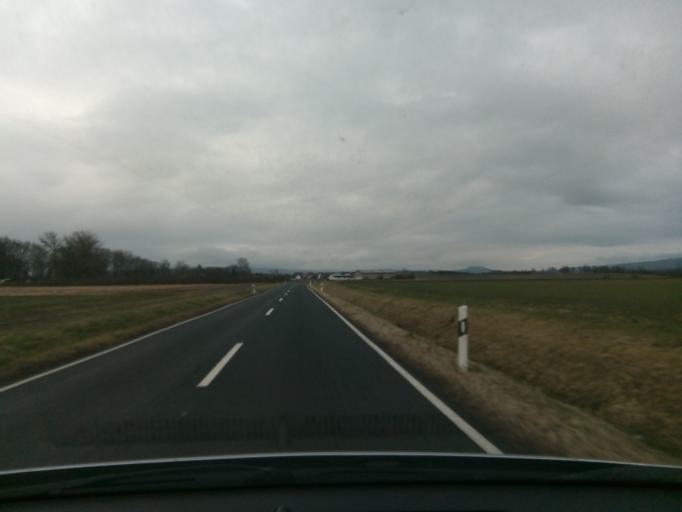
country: DE
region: Bavaria
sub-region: Regierungsbezirk Unterfranken
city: Sulzheim
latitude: 49.9331
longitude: 10.3491
